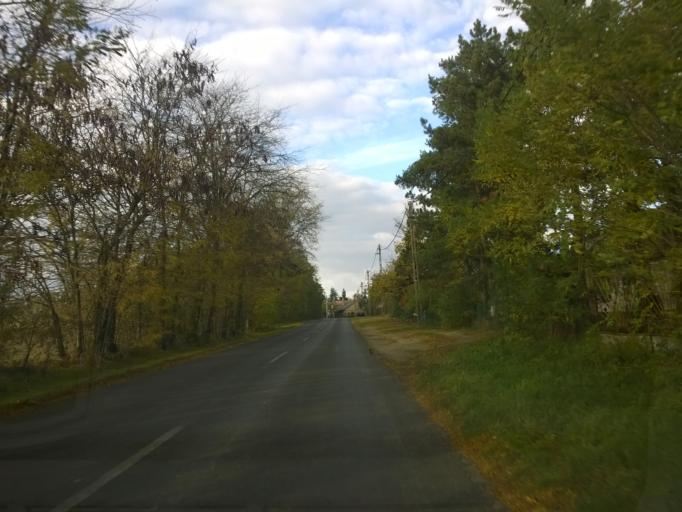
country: HU
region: Pest
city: Szigetcsep
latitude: 47.2467
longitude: 18.9638
